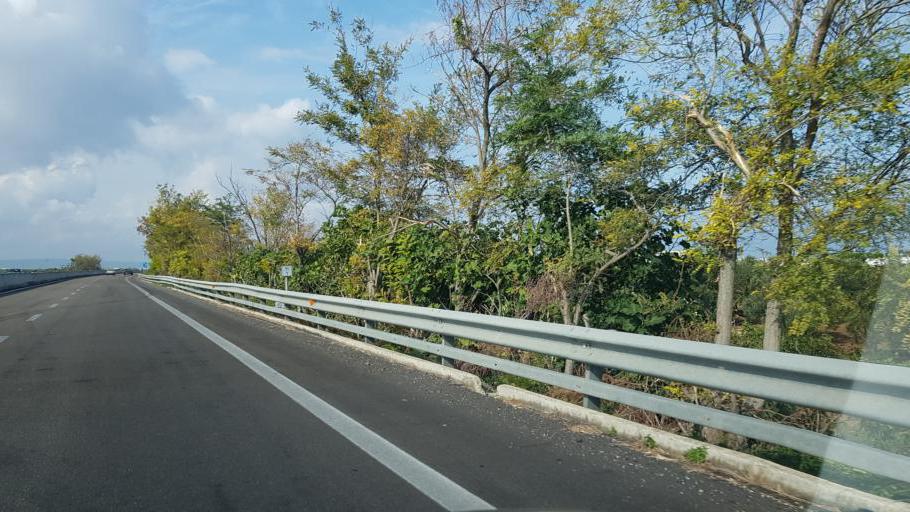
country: IT
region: Apulia
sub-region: Provincia di Brindisi
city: Montalbano
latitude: 40.8259
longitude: 17.4743
